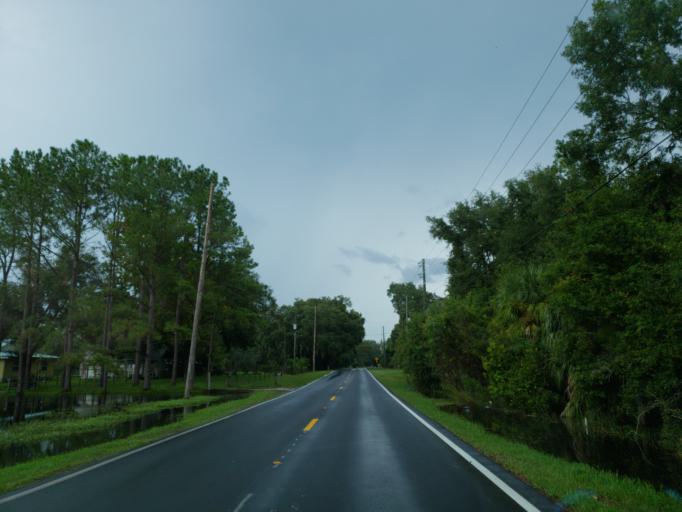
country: US
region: Florida
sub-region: Pasco County
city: Land O' Lakes
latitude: 28.2810
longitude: -82.4359
